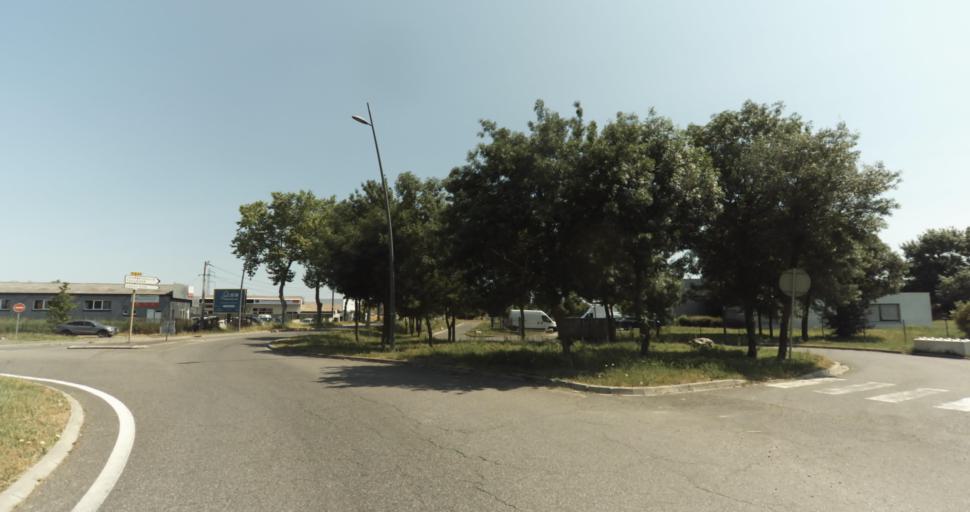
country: FR
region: Midi-Pyrenees
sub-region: Departement de la Haute-Garonne
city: La Salvetat-Saint-Gilles
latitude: 43.5578
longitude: 1.2782
